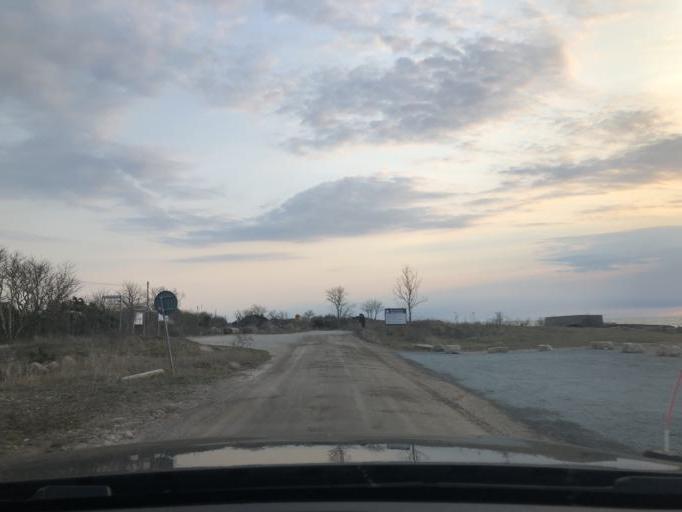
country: SE
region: Kalmar
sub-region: Borgholms Kommun
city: Borgholm
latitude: 57.2155
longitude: 16.9447
